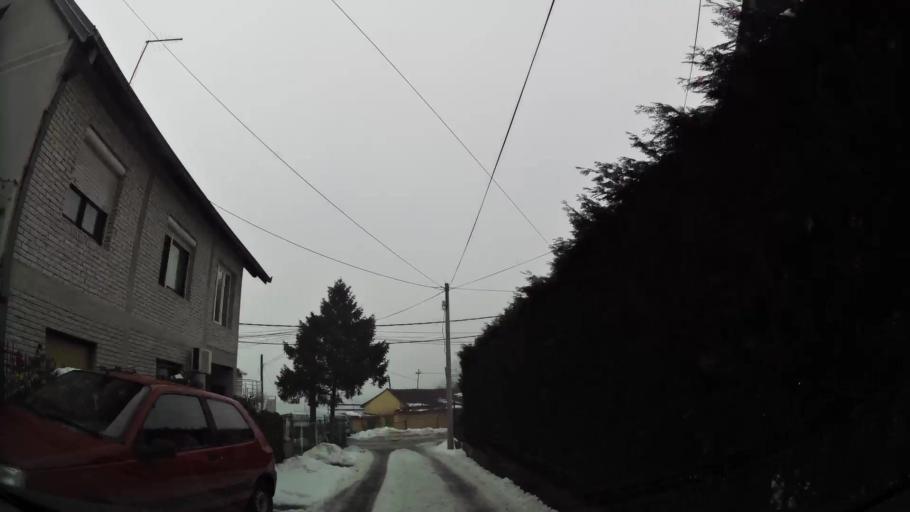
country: RS
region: Central Serbia
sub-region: Belgrade
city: Zvezdara
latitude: 44.7802
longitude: 20.5307
